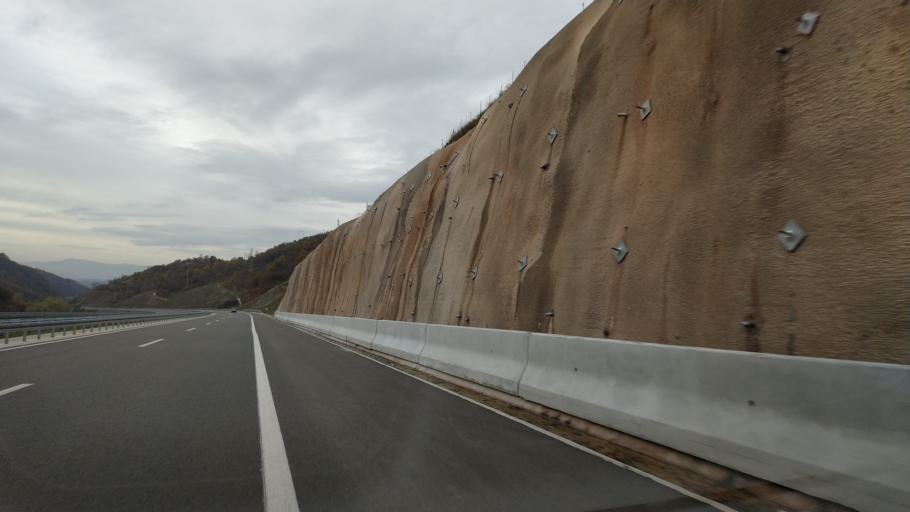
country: RS
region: Central Serbia
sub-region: Nisavski Okrug
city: Niska Banja
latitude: 43.2946
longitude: 22.0934
